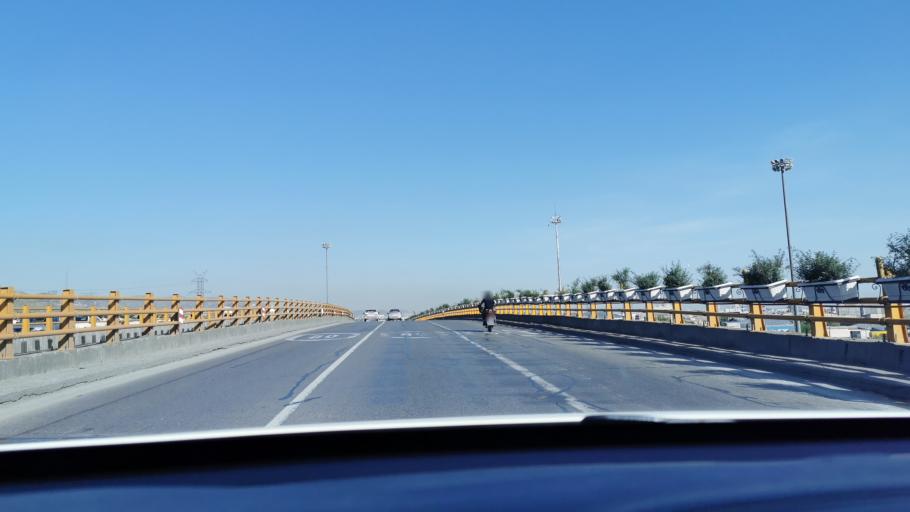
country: IR
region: Razavi Khorasan
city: Mashhad
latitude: 36.2555
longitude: 59.6000
